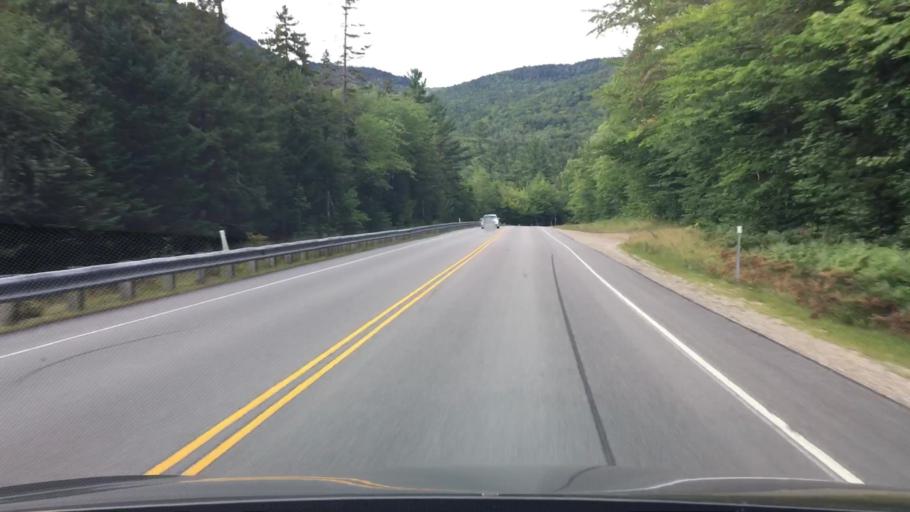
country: US
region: New Hampshire
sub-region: Carroll County
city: Tamworth
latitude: 44.0041
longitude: -71.2773
